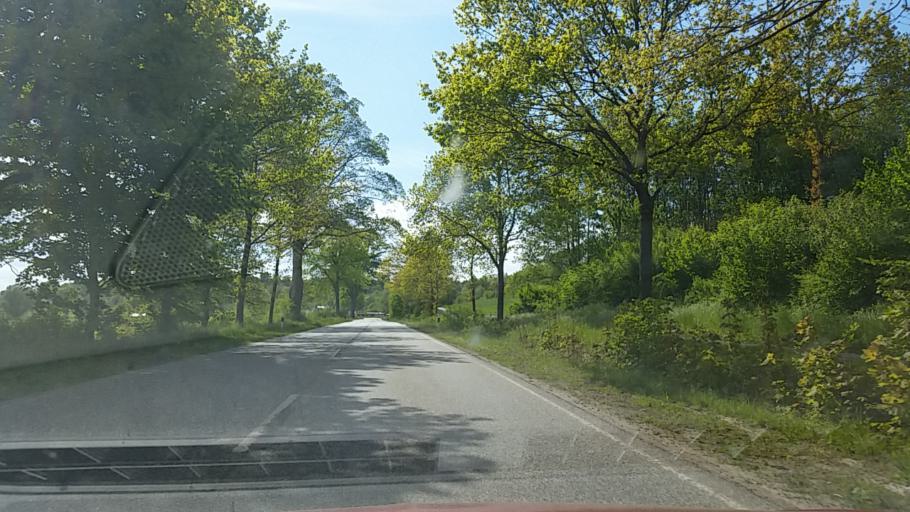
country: DE
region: Schleswig-Holstein
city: Meddewade
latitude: 53.8206
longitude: 10.4393
